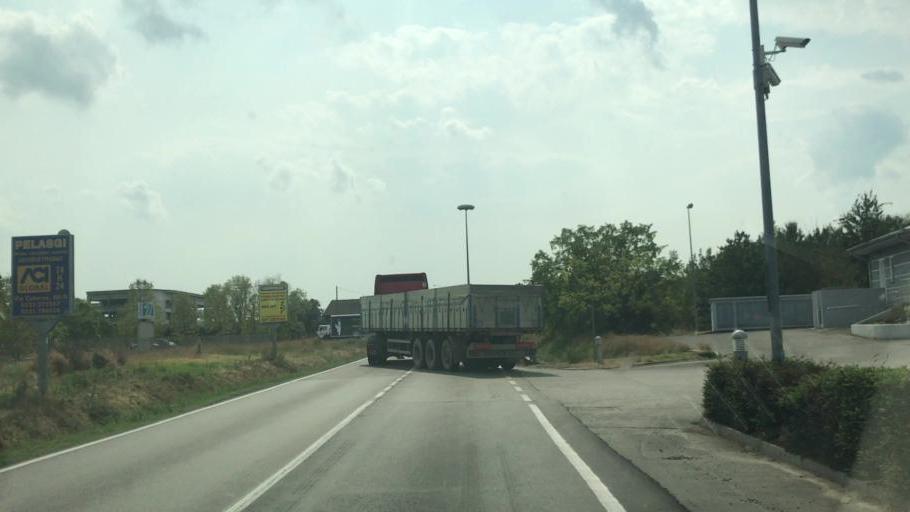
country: IT
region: Emilia-Romagna
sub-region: Provincia di Parma
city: Baganzola
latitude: 44.8494
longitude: 10.3415
